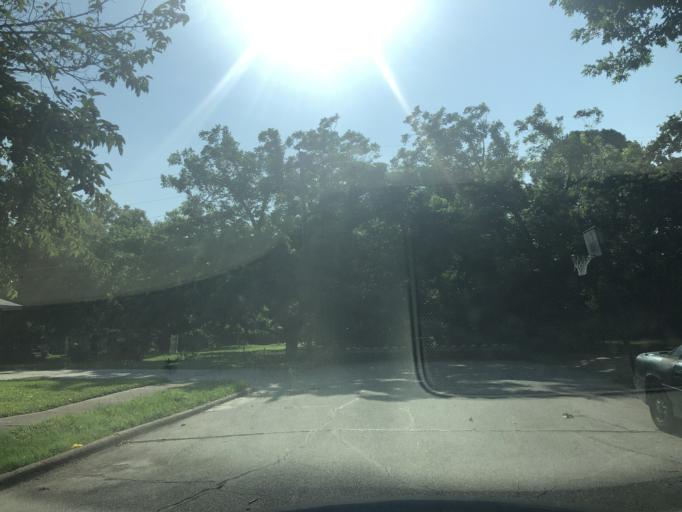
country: US
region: Texas
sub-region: Dallas County
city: Irving
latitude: 32.8116
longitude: -96.9880
